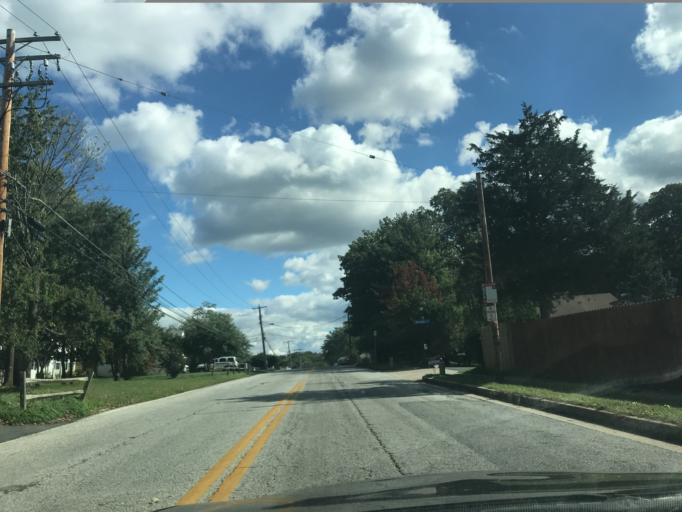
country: US
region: Maryland
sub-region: Baltimore County
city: Rossville
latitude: 39.3561
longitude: -76.4664
